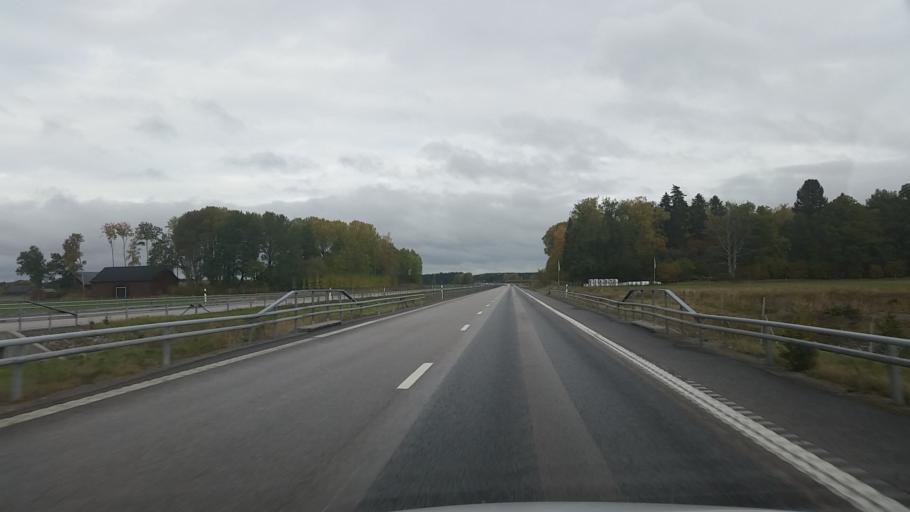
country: SE
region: Uppsala
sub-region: Osthammars Kommun
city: Bjorklinge
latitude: 60.0600
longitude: 17.6131
